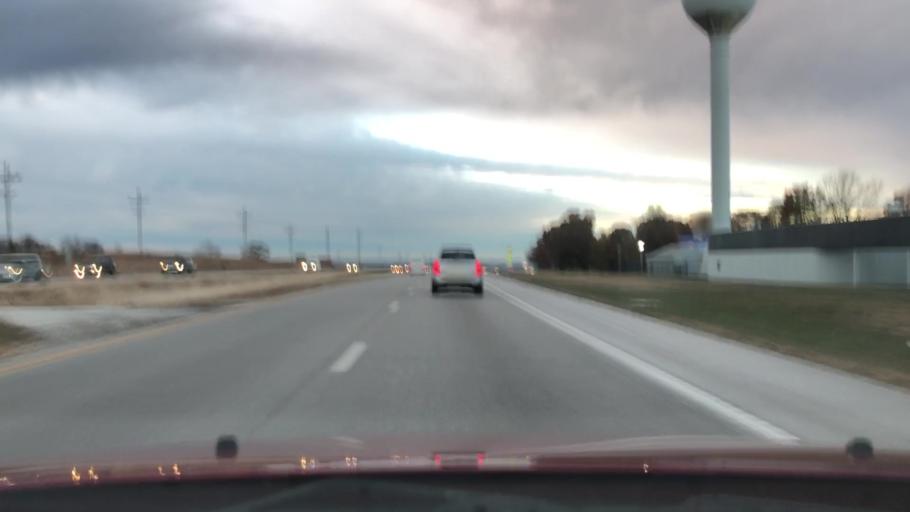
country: US
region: Missouri
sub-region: Christian County
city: Ozark
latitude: 37.0516
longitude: -93.2267
